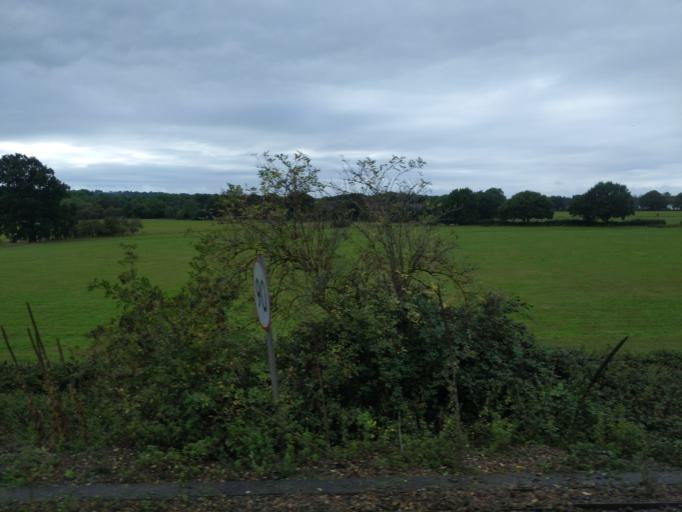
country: GB
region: England
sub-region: Kent
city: Tonbridge
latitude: 51.2036
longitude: 0.2534
